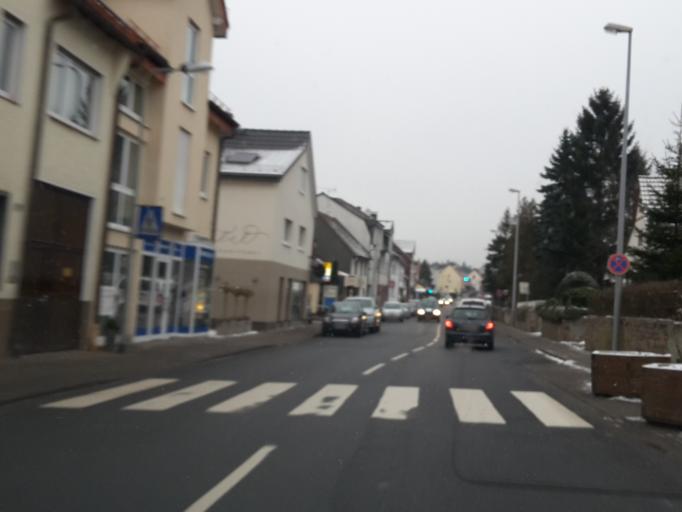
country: DE
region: Hesse
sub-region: Regierungsbezirk Darmstadt
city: Glashutten
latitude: 50.2168
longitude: 8.4029
